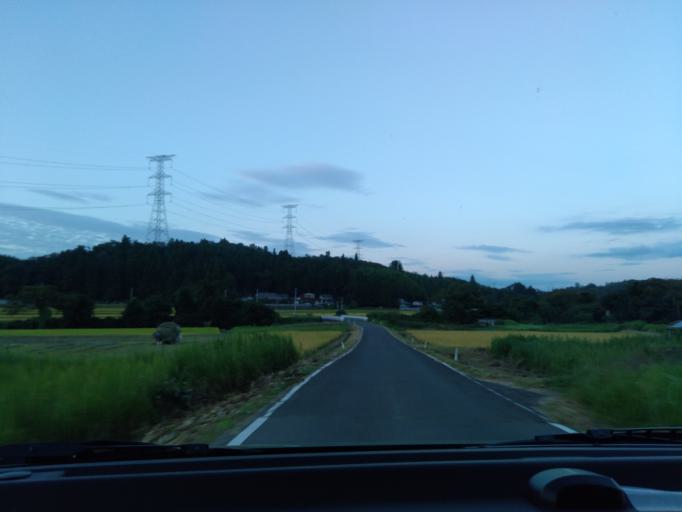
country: JP
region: Iwate
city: Ichinoseki
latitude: 38.8590
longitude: 141.1439
